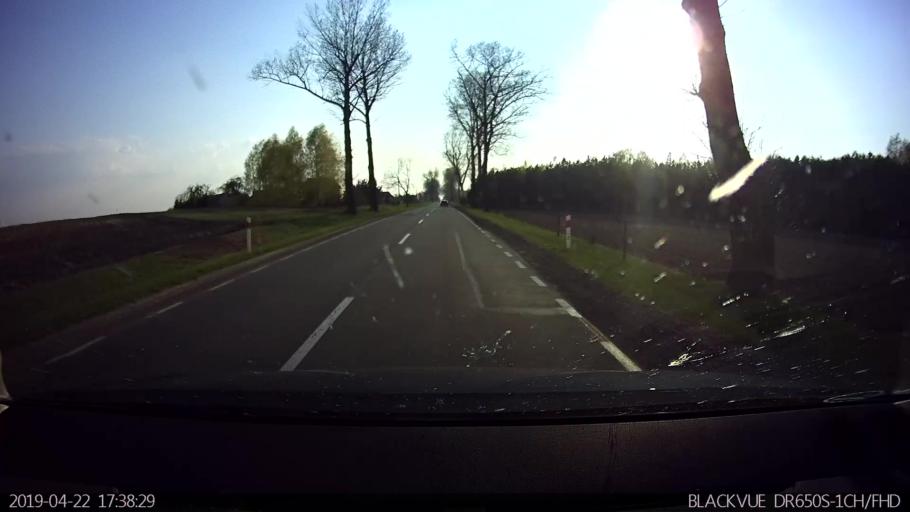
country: PL
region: Masovian Voivodeship
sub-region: Powiat wegrowski
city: Miedzna
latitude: 52.4086
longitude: 22.1605
